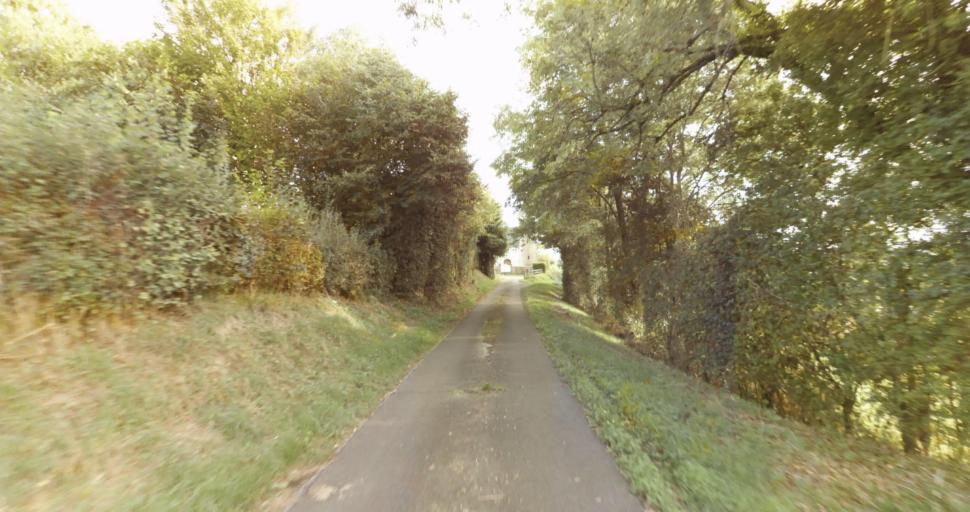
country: FR
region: Lower Normandy
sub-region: Departement de l'Orne
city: Gace
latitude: 48.7322
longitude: 0.2695
